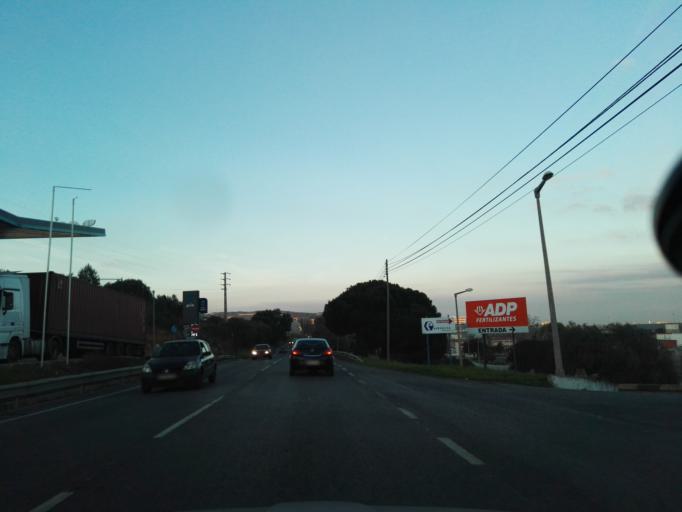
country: PT
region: Lisbon
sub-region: Vila Franca de Xira
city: Vialonga
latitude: 38.8792
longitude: -9.0514
